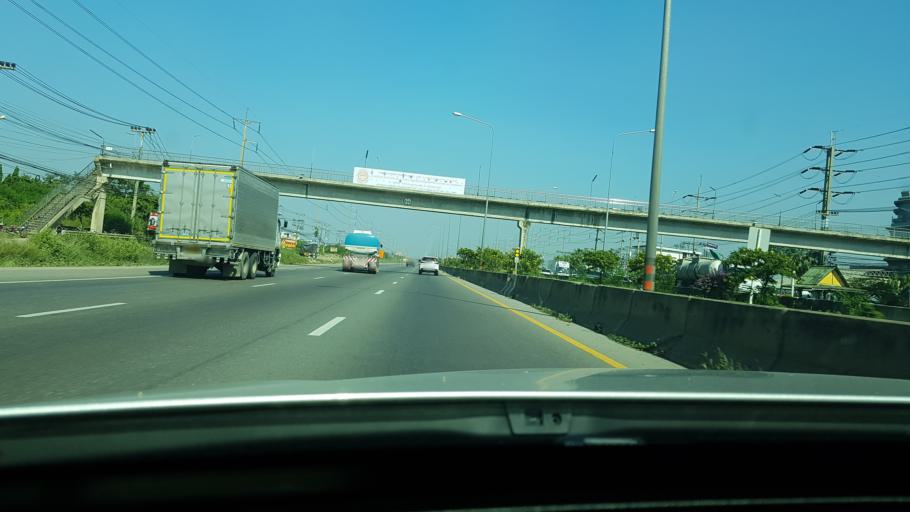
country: TH
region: Samut Sakhon
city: Ban Phaeo
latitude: 13.5153
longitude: 100.1558
